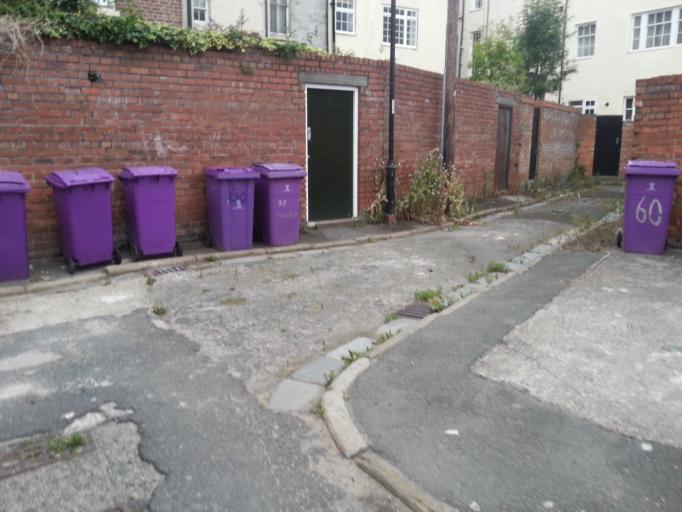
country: GB
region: England
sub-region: Liverpool
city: Liverpool
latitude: 53.3992
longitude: -2.9671
